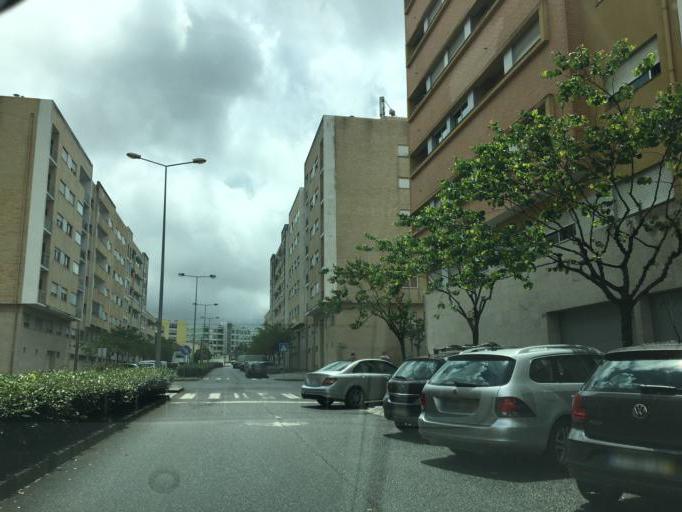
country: PT
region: Porto
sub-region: Maia
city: Anta
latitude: 41.2664
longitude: -8.6146
